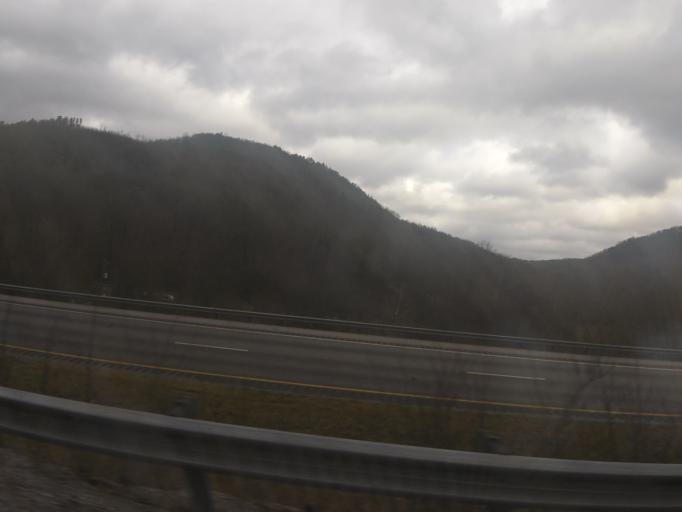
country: US
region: Georgia
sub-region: Walker County
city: Lookout Mountain
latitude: 34.9908
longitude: -85.4730
